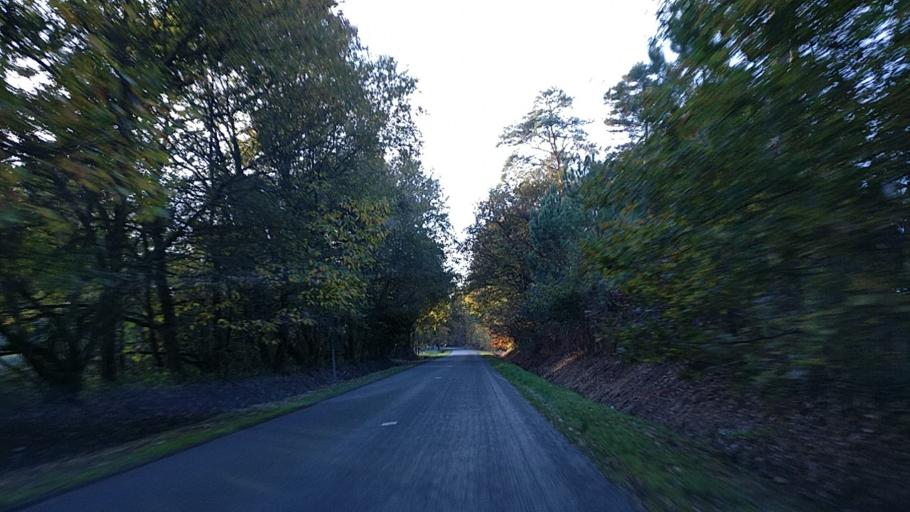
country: FR
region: Brittany
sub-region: Departement d'Ille-et-Vilaine
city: Liffre
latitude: 48.1894
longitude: -1.5255
